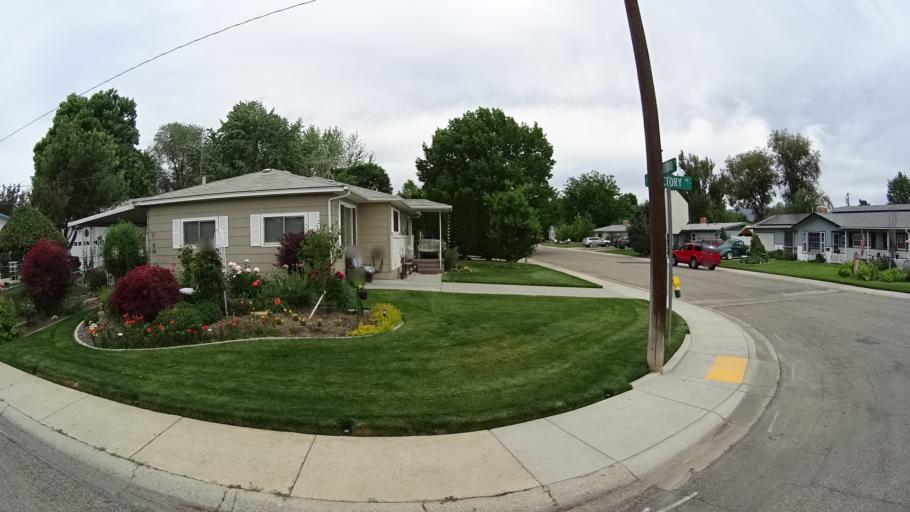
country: US
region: Idaho
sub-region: Ada County
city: Boise
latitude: 43.5754
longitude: -116.2070
